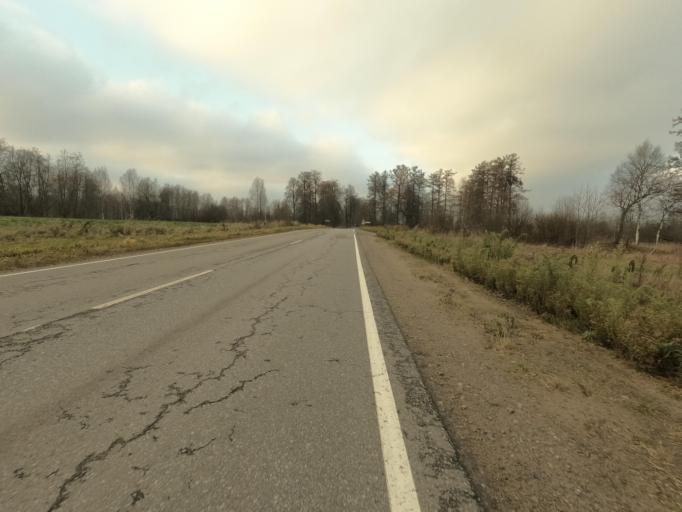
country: RU
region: Leningrad
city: Mga
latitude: 59.7711
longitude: 31.0227
